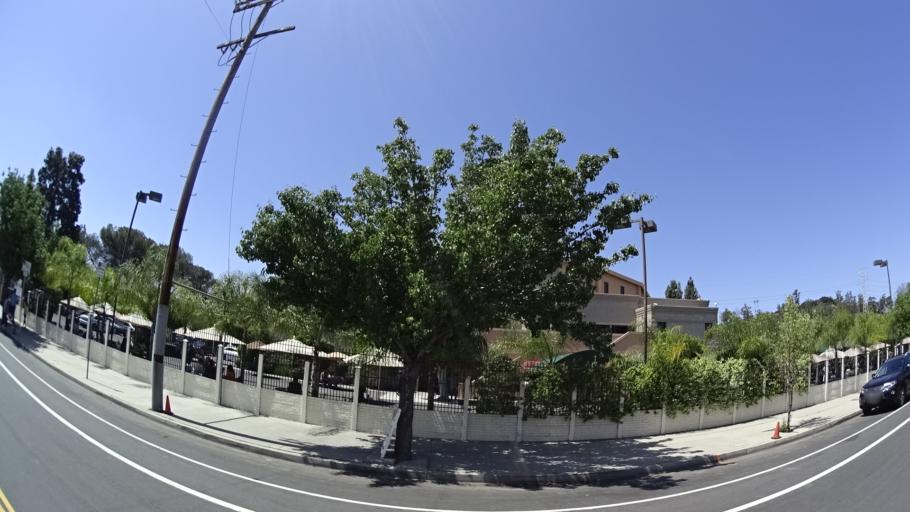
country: US
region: California
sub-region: Los Angeles County
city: Los Angeles
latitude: 34.0725
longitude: -118.2230
